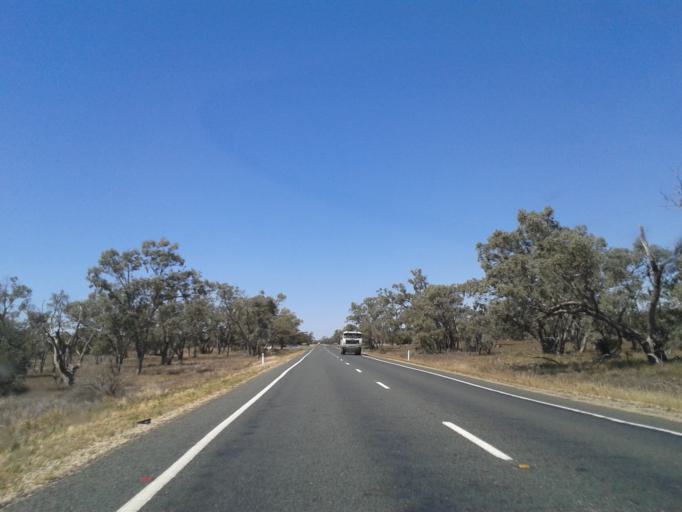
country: AU
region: New South Wales
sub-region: Wentworth
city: Gol Gol
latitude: -34.5378
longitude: 142.6497
